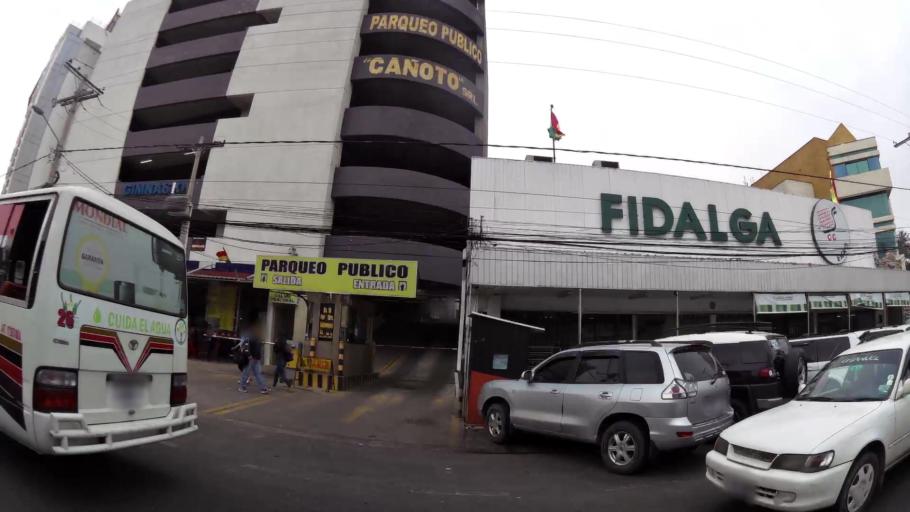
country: BO
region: Santa Cruz
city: Santa Cruz de la Sierra
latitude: -17.7790
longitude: -63.1885
